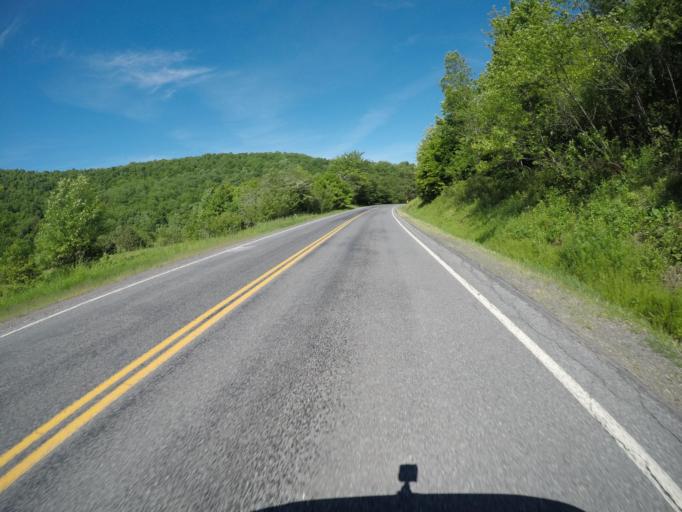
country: US
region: New York
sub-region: Delaware County
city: Delhi
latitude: 42.2113
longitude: -74.8705
